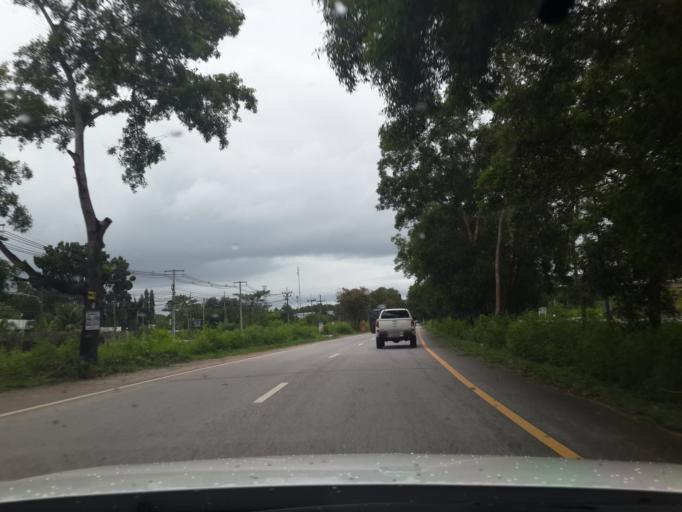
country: TH
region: Songkhla
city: Hat Yai
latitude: 6.9719
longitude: 100.4937
